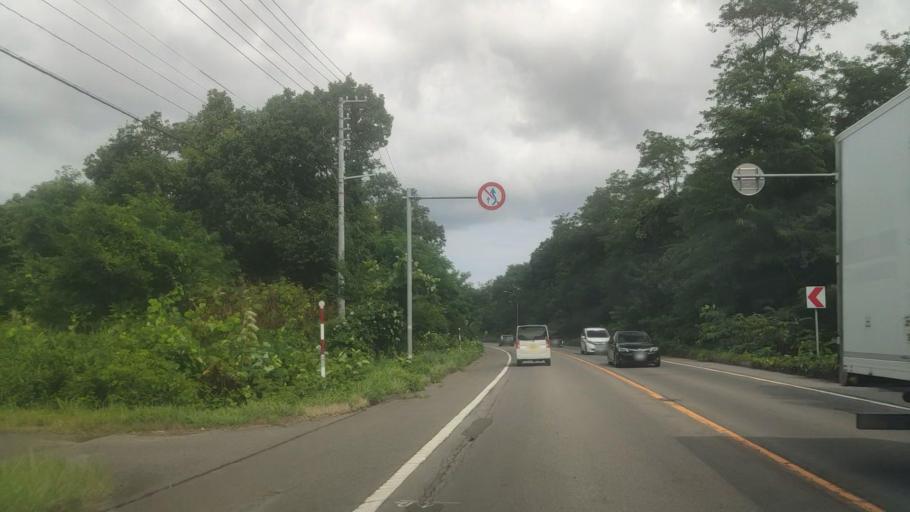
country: JP
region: Hokkaido
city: Nanae
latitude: 42.0705
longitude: 140.6030
